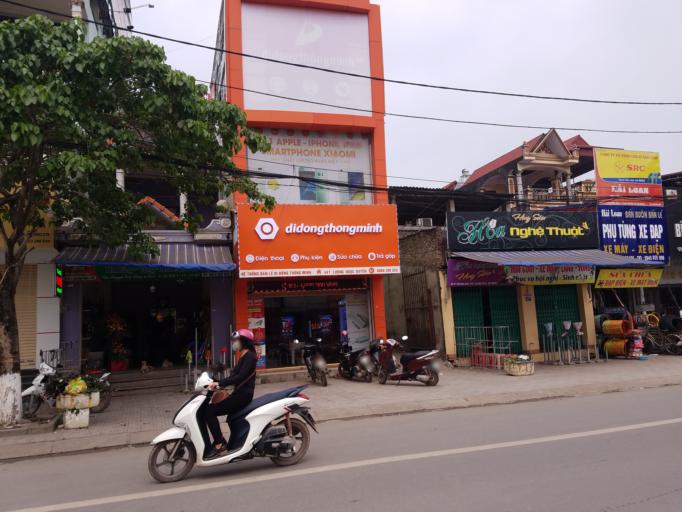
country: VN
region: Thai Nguyen
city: Thanh Pho Thai Nguyen
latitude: 21.5888
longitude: 105.8282
